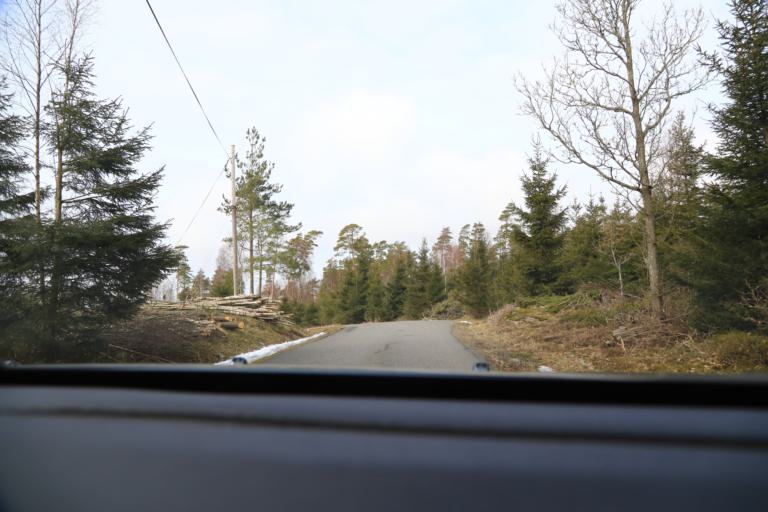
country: SE
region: Halland
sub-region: Varbergs Kommun
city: Veddige
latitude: 57.2151
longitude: 12.2454
